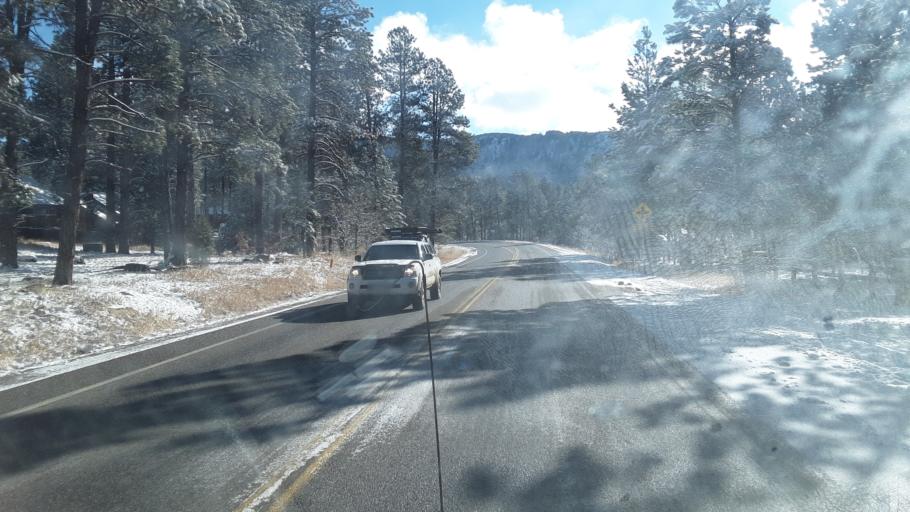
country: US
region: Colorado
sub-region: La Plata County
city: Durango
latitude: 37.3123
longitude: -107.7882
